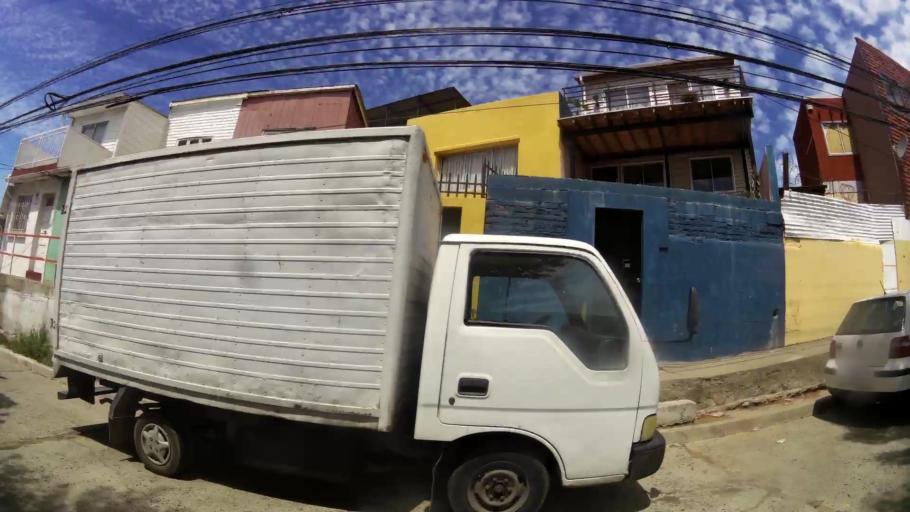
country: CL
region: Valparaiso
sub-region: Provincia de Valparaiso
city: Vina del Mar
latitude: -33.0372
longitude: -71.5845
